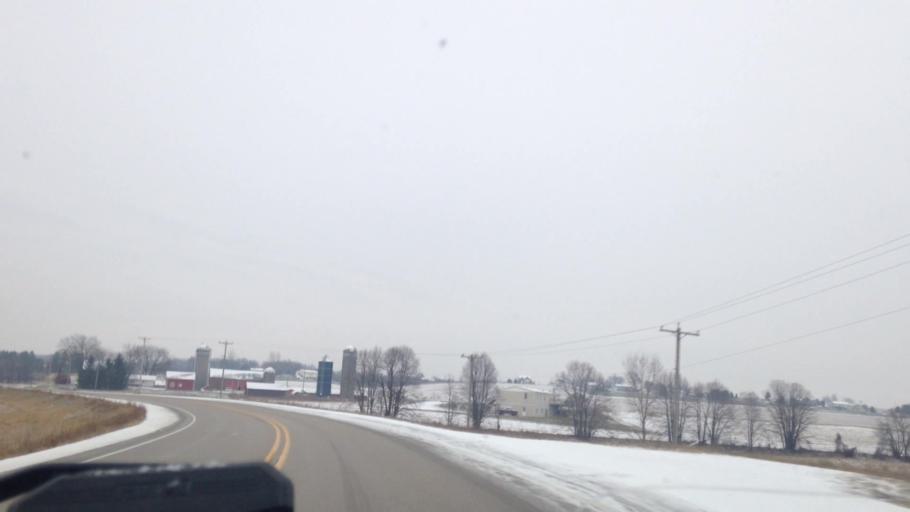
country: US
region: Wisconsin
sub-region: Dodge County
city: Hustisford
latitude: 43.3702
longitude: -88.5385
